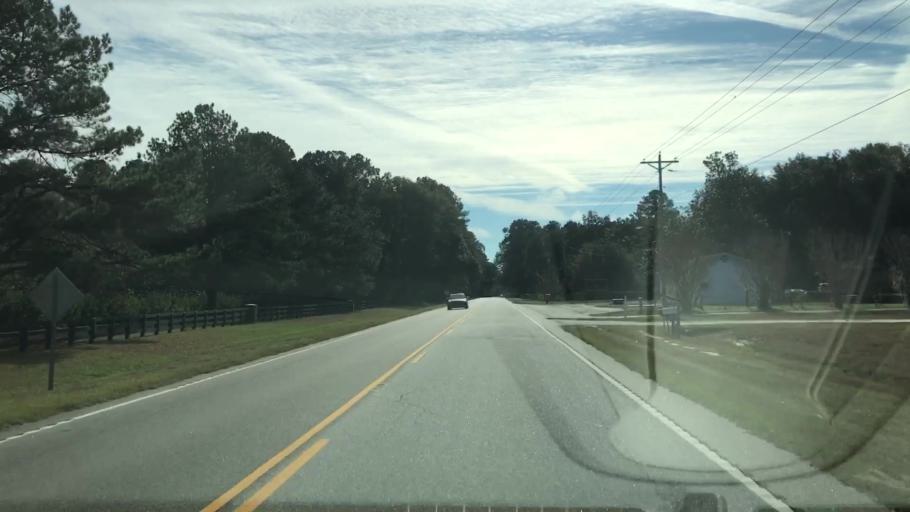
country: US
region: South Carolina
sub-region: Colleton County
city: Walterboro
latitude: 32.8562
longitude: -80.5989
